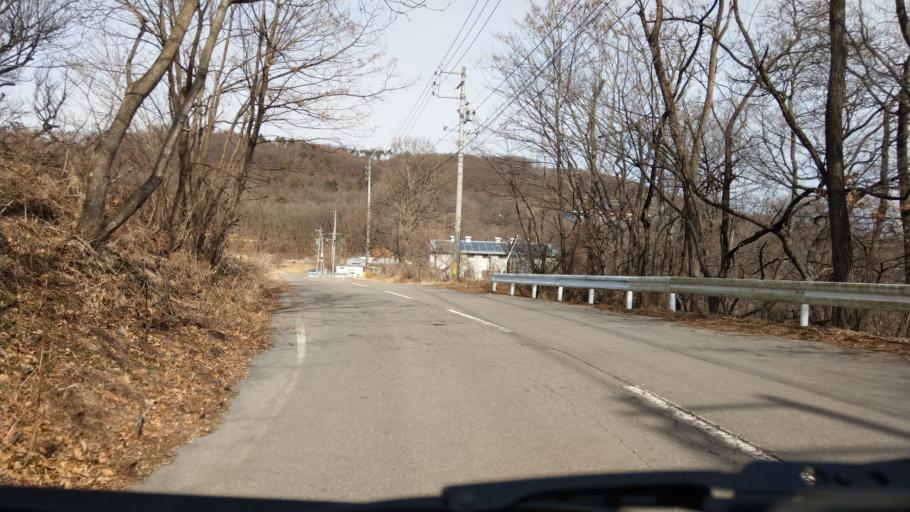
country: JP
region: Nagano
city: Komoro
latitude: 36.2839
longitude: 138.4059
